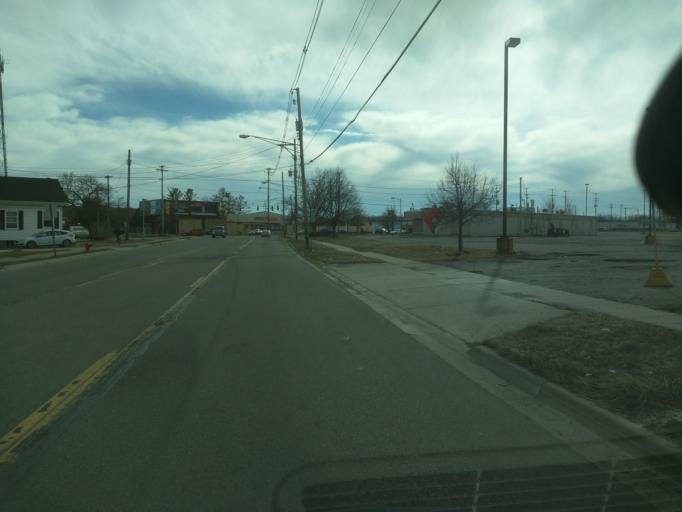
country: US
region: Michigan
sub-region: Ingham County
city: Lansing
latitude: 42.6985
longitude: -84.5636
